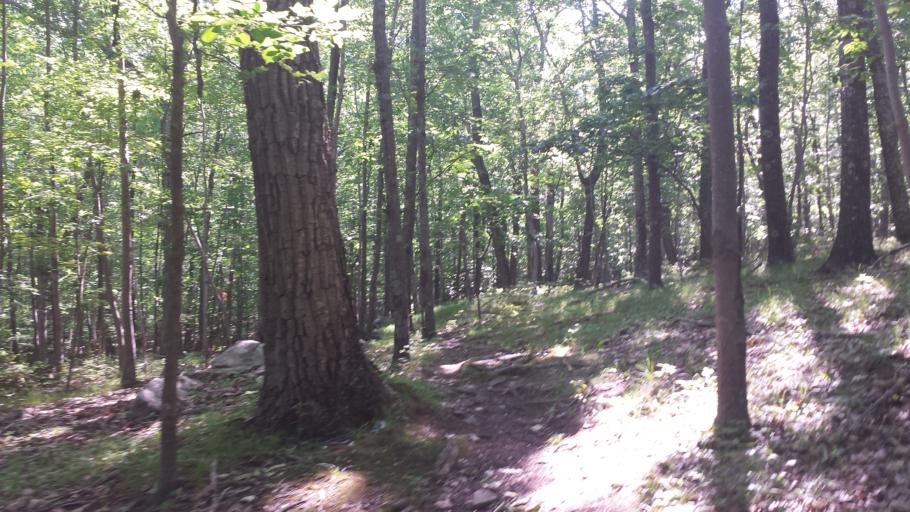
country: US
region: New York
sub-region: Putnam County
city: Peach Lake
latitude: 41.3100
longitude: -73.5567
